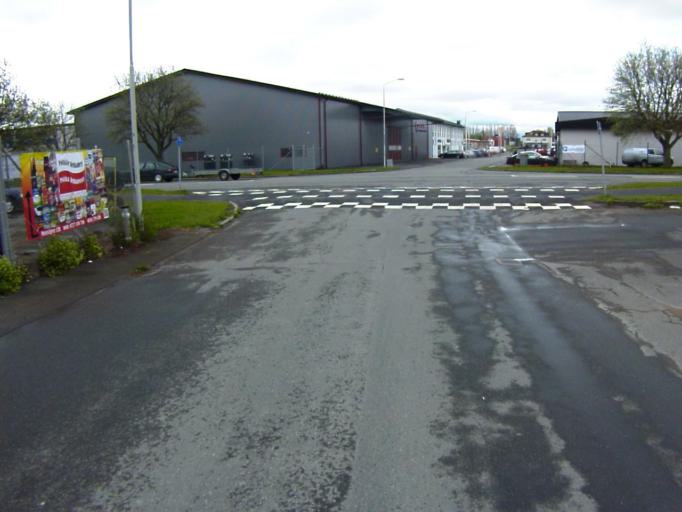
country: SE
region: Skane
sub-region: Kristianstads Kommun
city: Kristianstad
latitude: 56.0230
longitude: 14.1365
